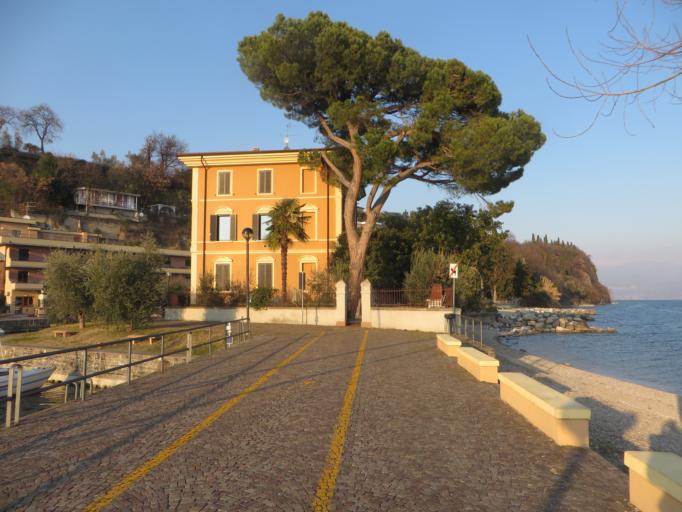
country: IT
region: Lombardy
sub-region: Provincia di Brescia
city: Solarolo
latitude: 45.5447
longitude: 10.5677
